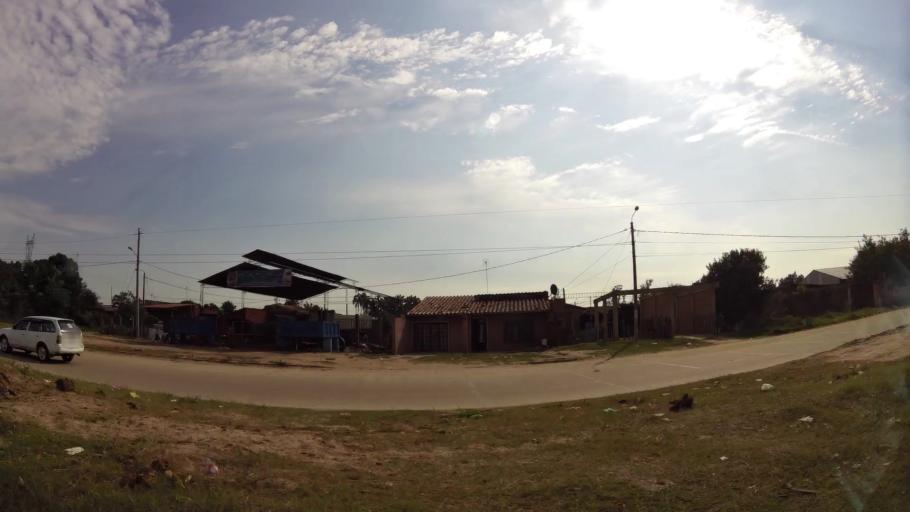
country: BO
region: Santa Cruz
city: Santa Cruz de la Sierra
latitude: -17.7286
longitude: -63.1346
